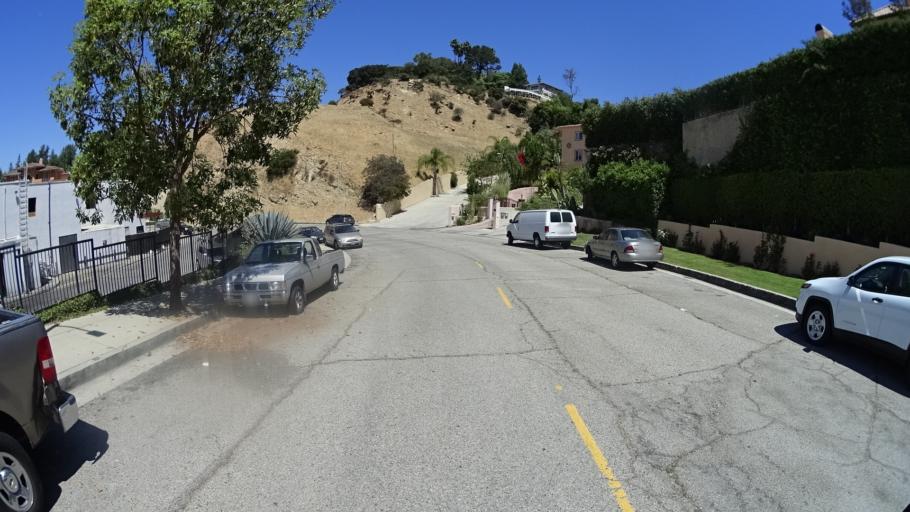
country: US
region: California
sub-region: Los Angeles County
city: Sherman Oaks
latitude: 34.1282
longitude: -118.4439
